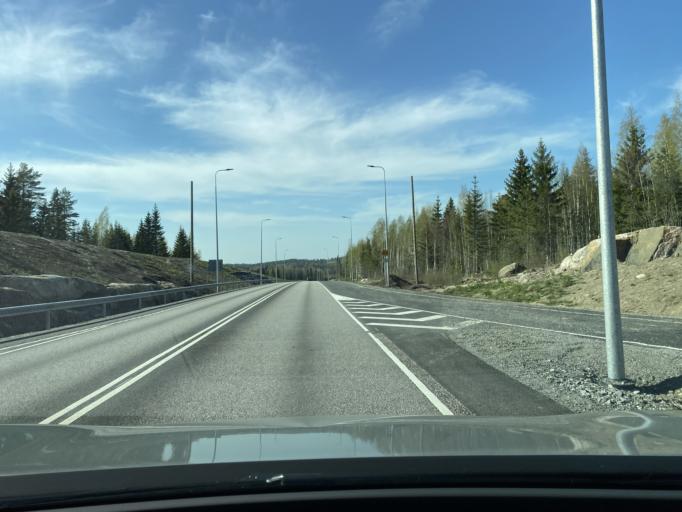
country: FI
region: Uusimaa
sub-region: Helsinki
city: Nurmijaervi
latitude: 60.3898
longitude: 24.7832
